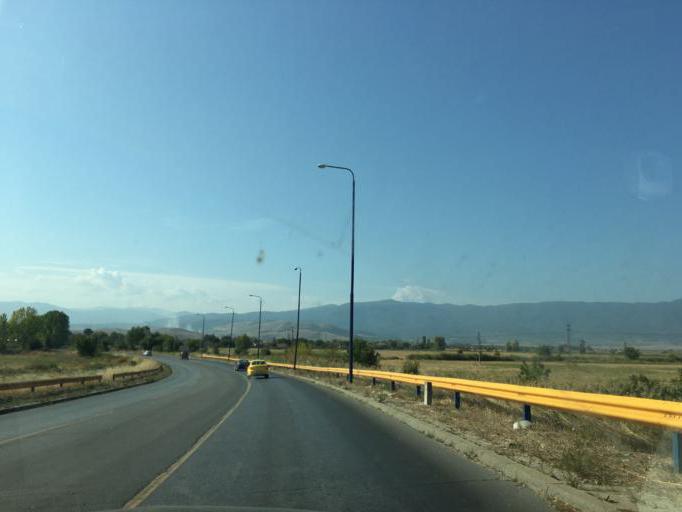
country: BG
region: Pazardzhik
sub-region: Obshtina Pazardzhik
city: Pazardzhik
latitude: 42.1697
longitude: 24.3153
